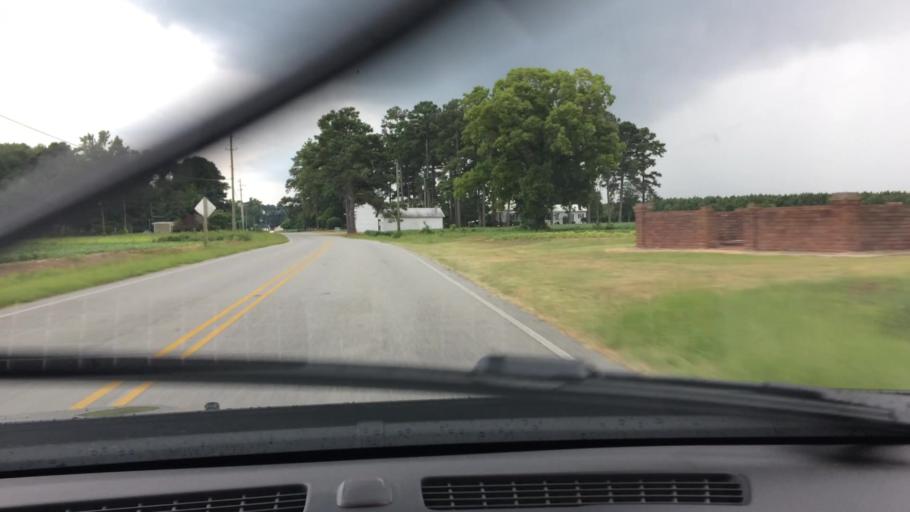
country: US
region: North Carolina
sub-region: Pitt County
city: Ayden
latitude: 35.4831
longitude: -77.3764
